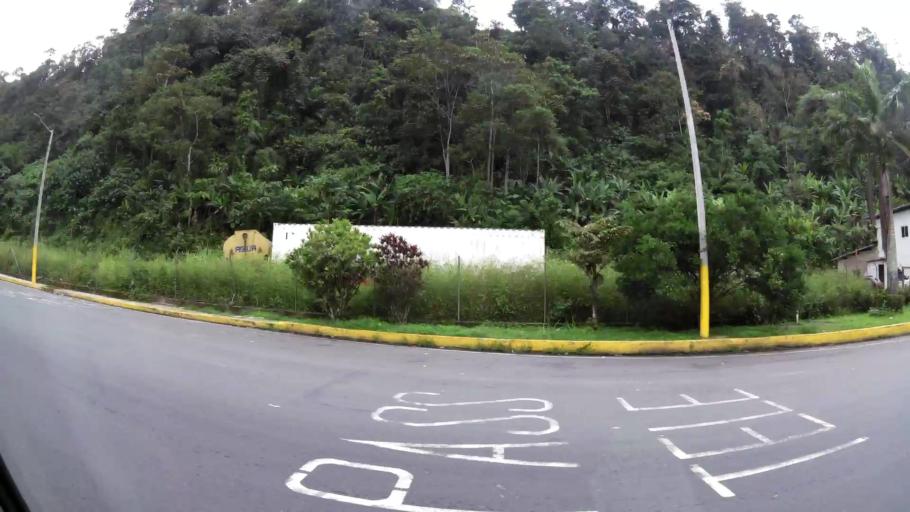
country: EC
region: Santo Domingo de los Tsachilas
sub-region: Canton Santo Domingo de los Colorados
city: Santo Domingo de los Colorados
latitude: -0.2750
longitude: -79.0785
